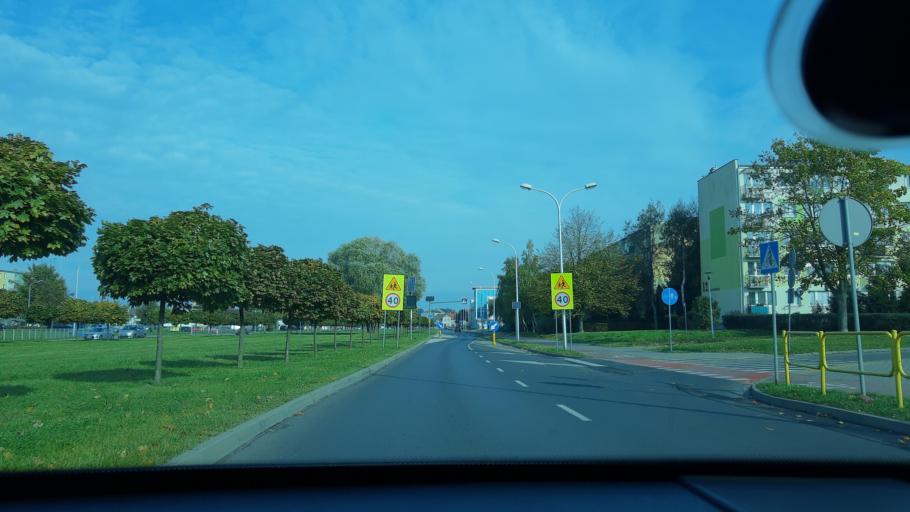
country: PL
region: Lodz Voivodeship
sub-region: Powiat sieradzki
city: Sieradz
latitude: 51.5915
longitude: 18.7151
